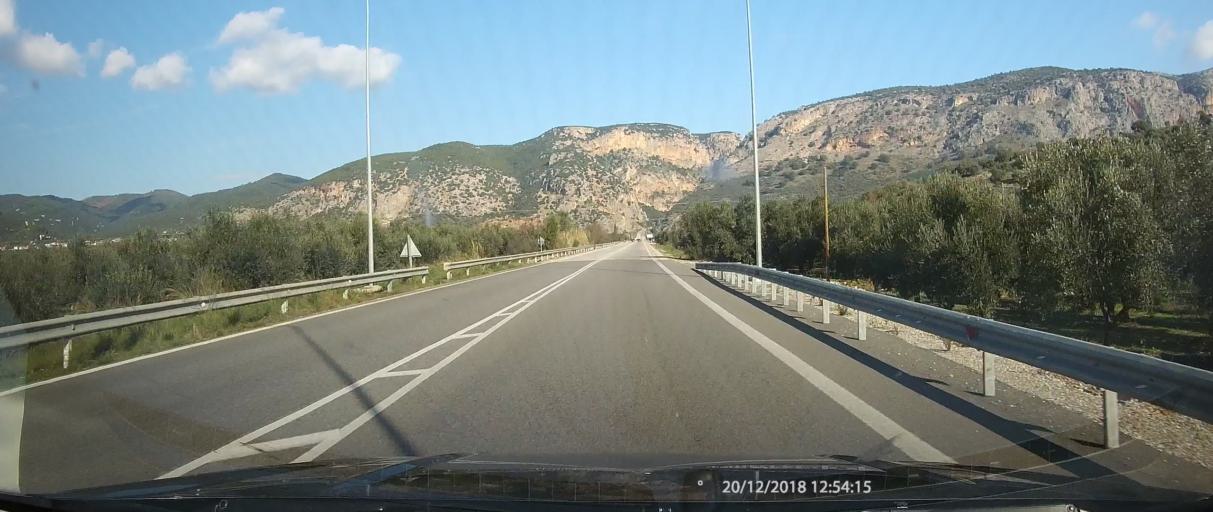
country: GR
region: West Greece
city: Aitoliko
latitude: 38.4870
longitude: 21.3538
